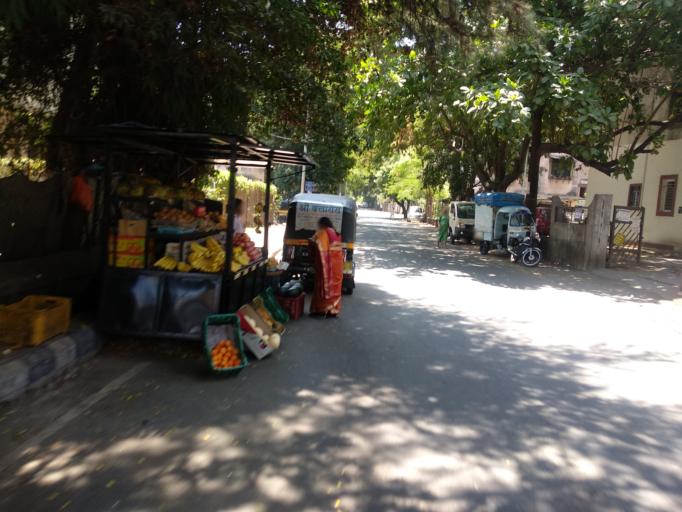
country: IN
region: Maharashtra
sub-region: Pune Division
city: Pune
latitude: 18.5045
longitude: 73.8452
